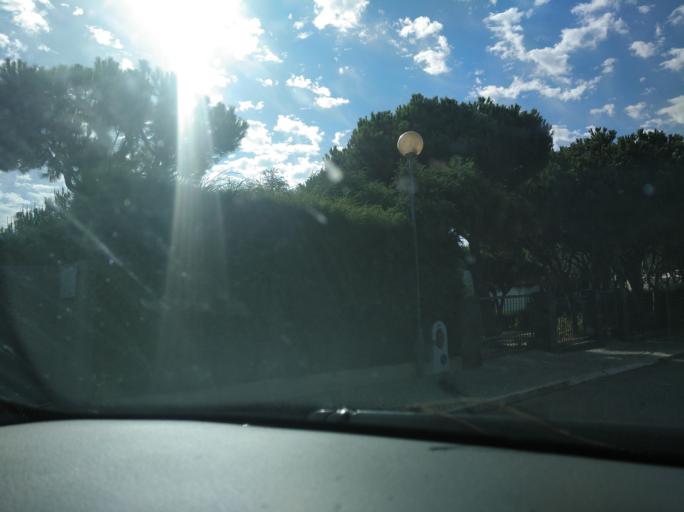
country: PT
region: Faro
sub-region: Vila Real de Santo Antonio
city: Monte Gordo
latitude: 37.1784
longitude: -7.4831
